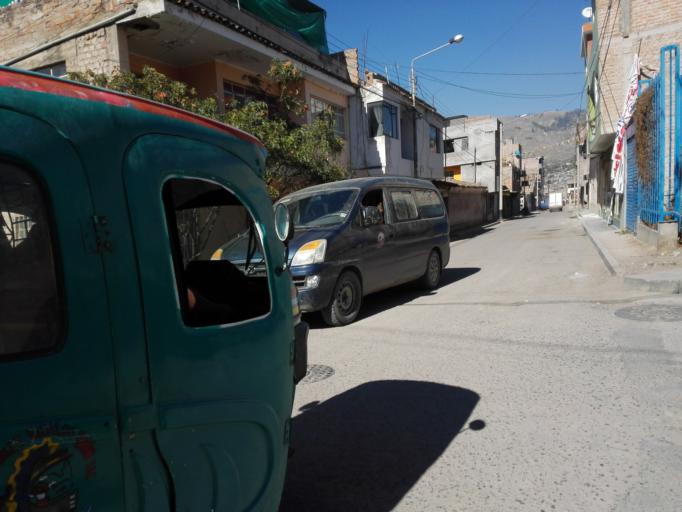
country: PE
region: Ayacucho
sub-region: Provincia de Huamanga
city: Ayacucho
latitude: -13.1550
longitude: -74.2167
